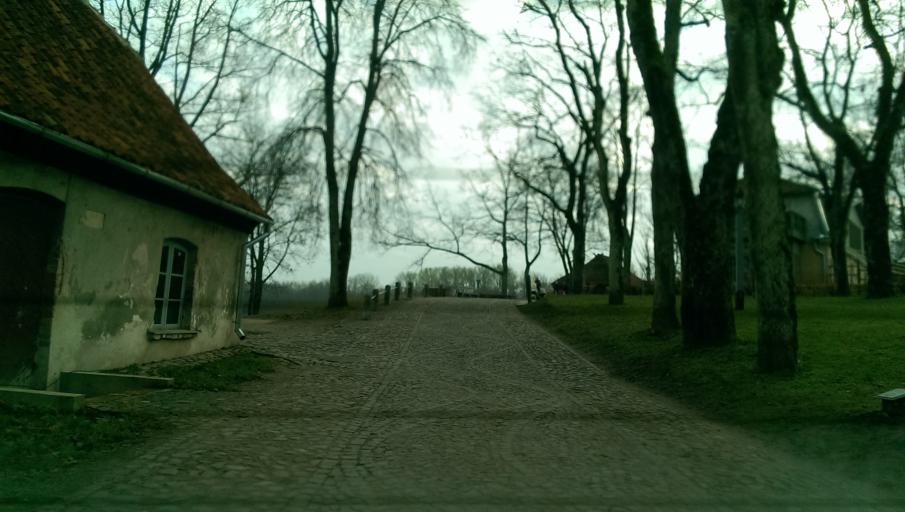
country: LV
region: Kuldigas Rajons
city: Kuldiga
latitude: 56.9693
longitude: 21.9763
